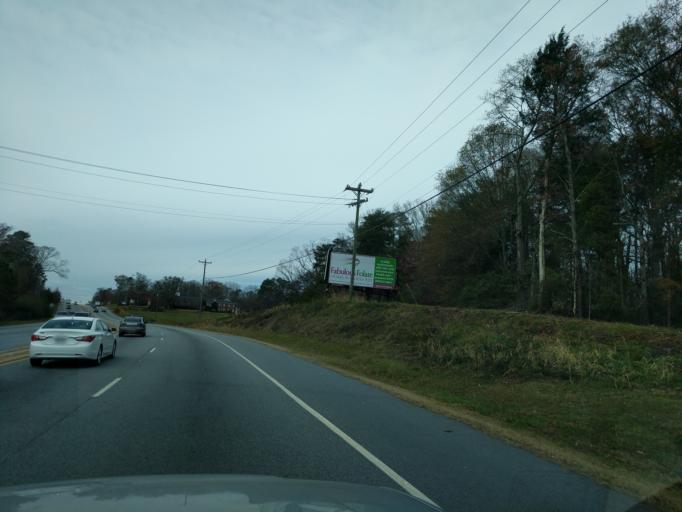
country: US
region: South Carolina
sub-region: Anderson County
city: Northlake
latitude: 34.5803
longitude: -82.7156
